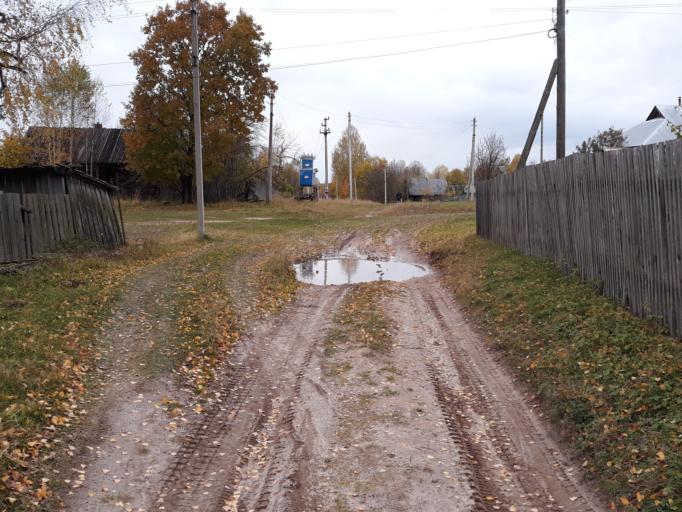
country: RU
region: Nizjnij Novgorod
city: Varnavino
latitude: 57.7141
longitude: 45.0213
